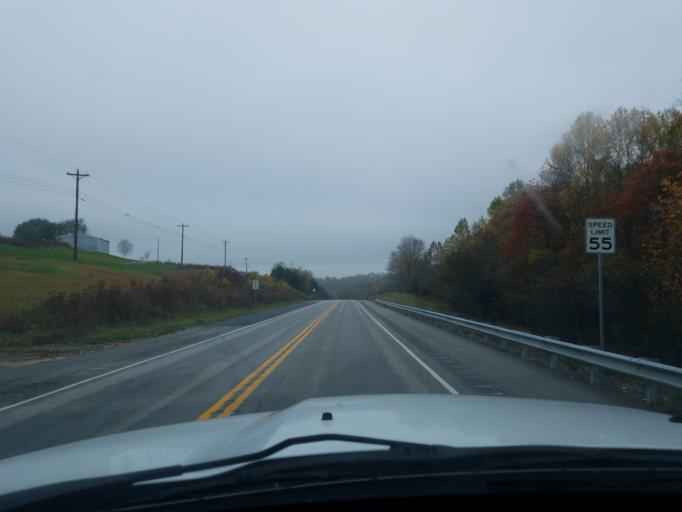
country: US
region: Kentucky
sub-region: Taylor County
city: Campbellsville
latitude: 37.3875
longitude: -85.4218
